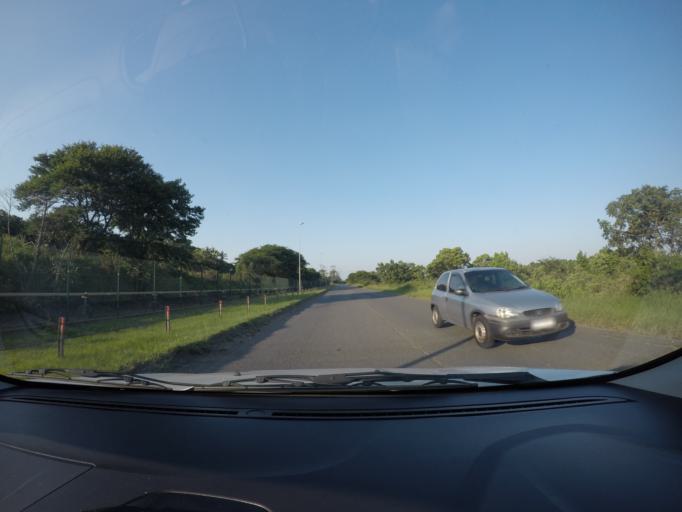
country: ZA
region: KwaZulu-Natal
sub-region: uThungulu District Municipality
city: Richards Bay
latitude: -28.7603
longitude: 32.0024
